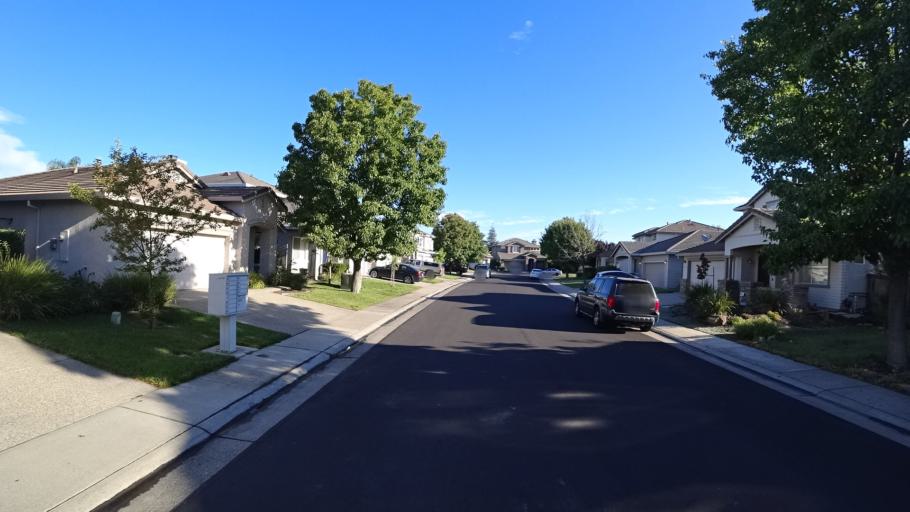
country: US
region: California
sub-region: Sacramento County
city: Laguna
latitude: 38.4038
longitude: -121.4759
